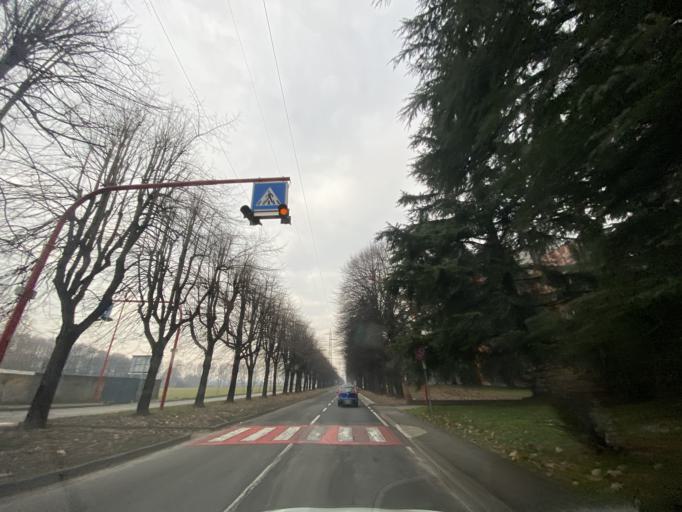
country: IT
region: Lombardy
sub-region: Citta metropolitana di Milano
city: Segrate
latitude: 45.4947
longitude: 9.2632
